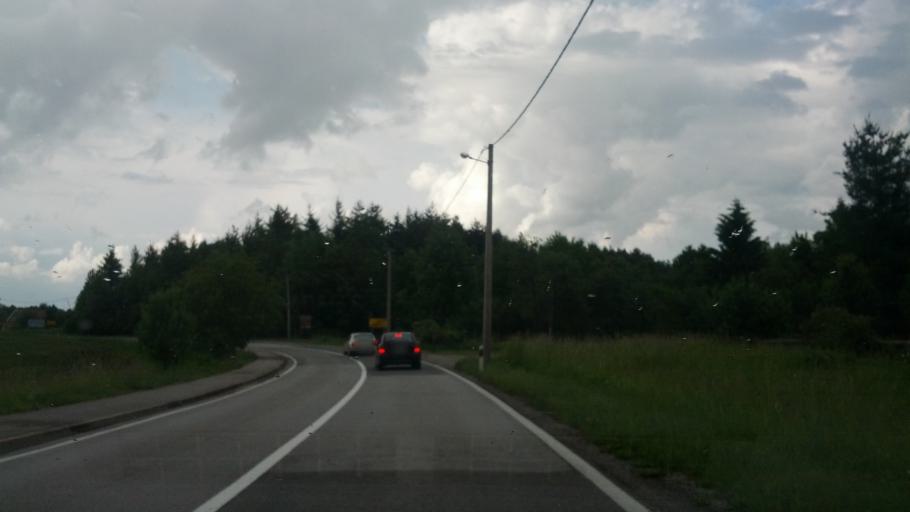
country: HR
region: Licko-Senjska
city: Jezerce
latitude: 44.9667
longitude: 15.6533
